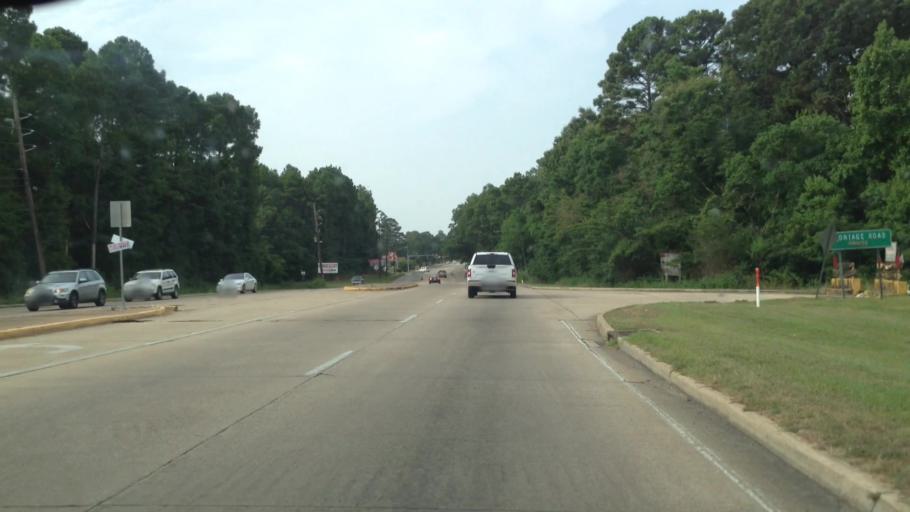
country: US
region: Louisiana
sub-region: Caddo Parish
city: Shreveport
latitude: 32.4159
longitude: -93.8148
